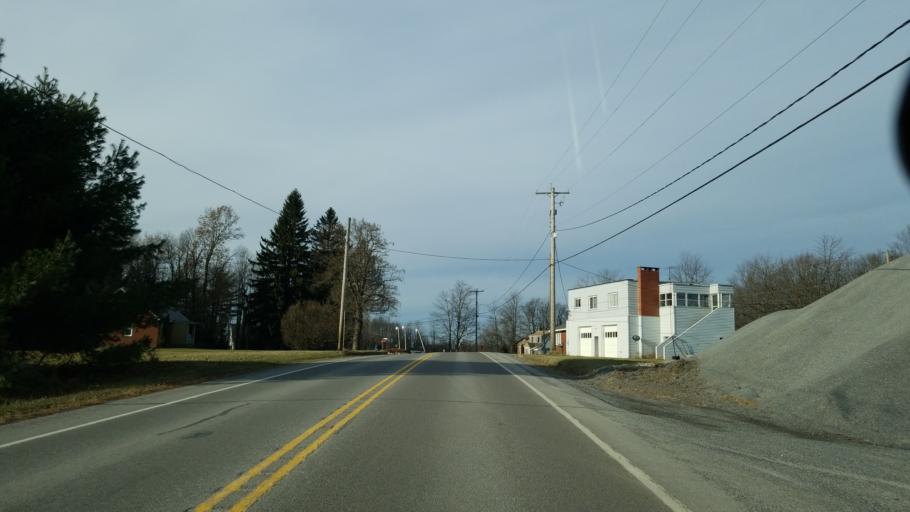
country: US
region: Pennsylvania
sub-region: Clearfield County
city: Curwensville
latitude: 41.0200
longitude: -78.6448
